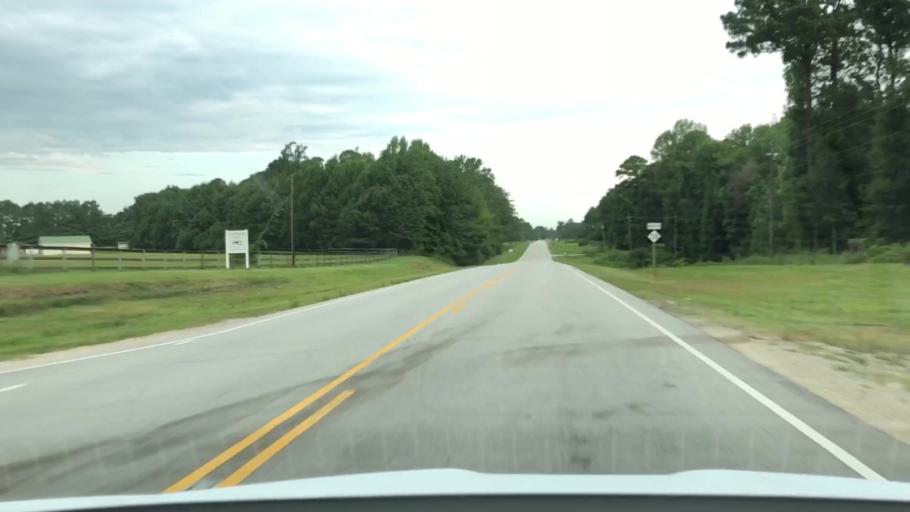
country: US
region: North Carolina
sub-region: Jones County
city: Trenton
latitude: 35.0115
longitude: -77.2897
